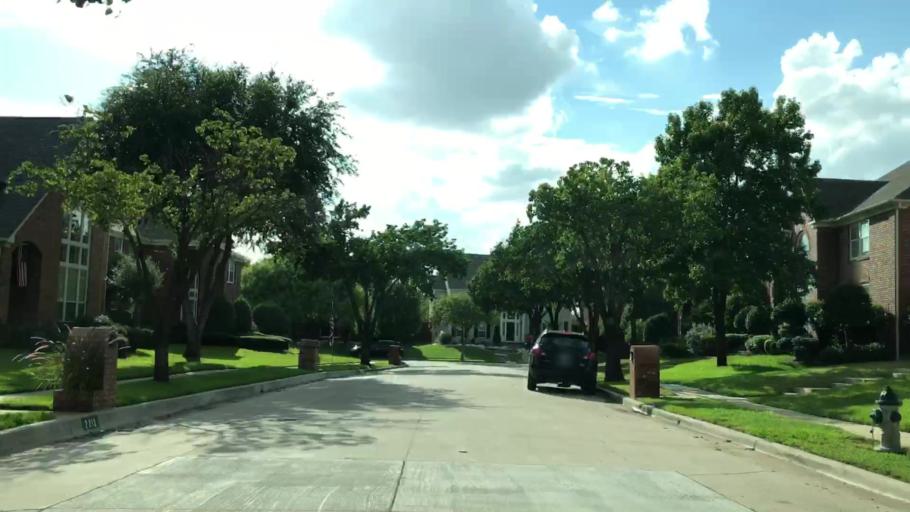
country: US
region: Texas
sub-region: Dallas County
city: Coppell
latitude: 32.9151
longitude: -96.9740
